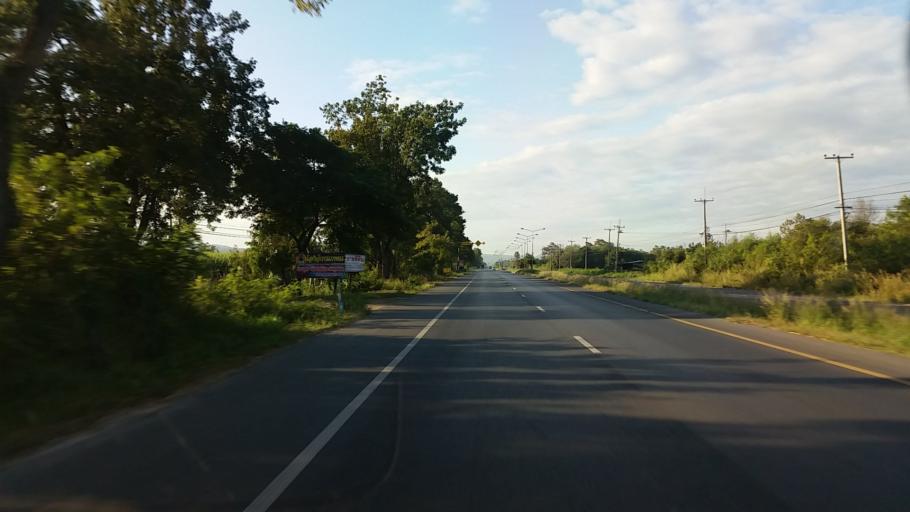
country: TH
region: Lop Buri
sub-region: Amphoe Tha Luang
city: Tha Luang
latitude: 15.0335
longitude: 100.9530
